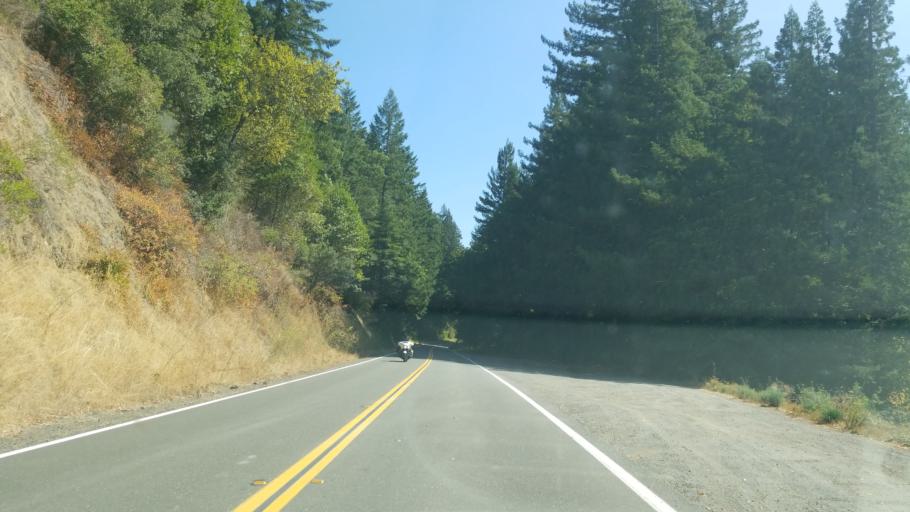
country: US
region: California
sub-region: Humboldt County
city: Redway
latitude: 40.3298
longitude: -123.9276
